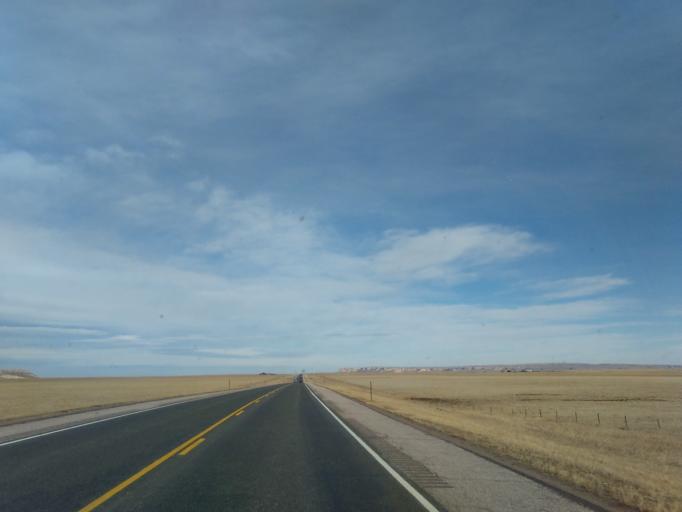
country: US
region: Wyoming
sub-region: Laramie County
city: Pine Bluffs
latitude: 41.5981
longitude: -104.2638
